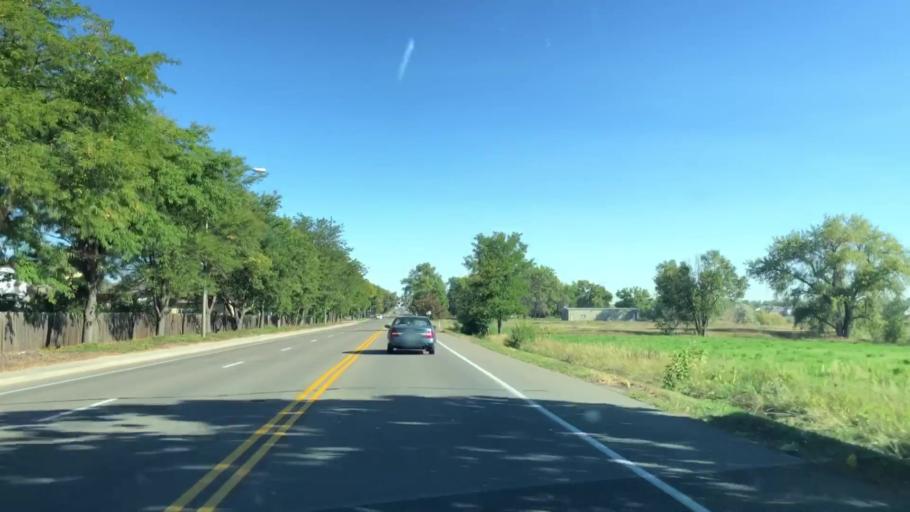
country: US
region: Colorado
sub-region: Larimer County
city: Loveland
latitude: 40.4187
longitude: -105.0587
